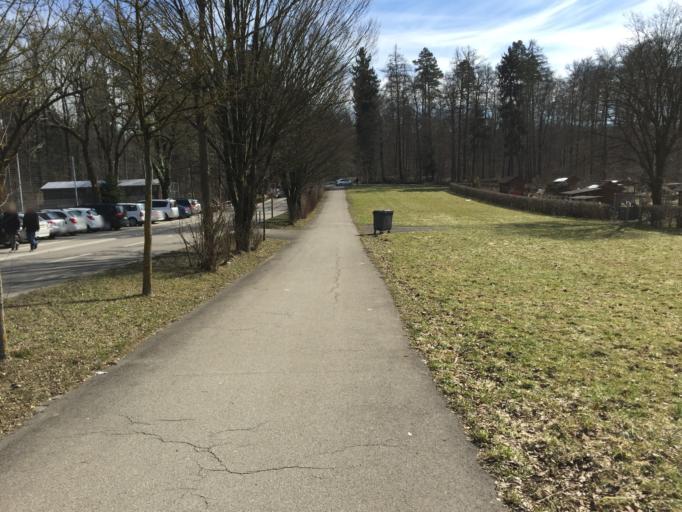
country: CH
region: Zurich
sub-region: Bezirk Zuerich
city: Zuerich (Kreis 7)
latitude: 47.3803
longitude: 8.5729
